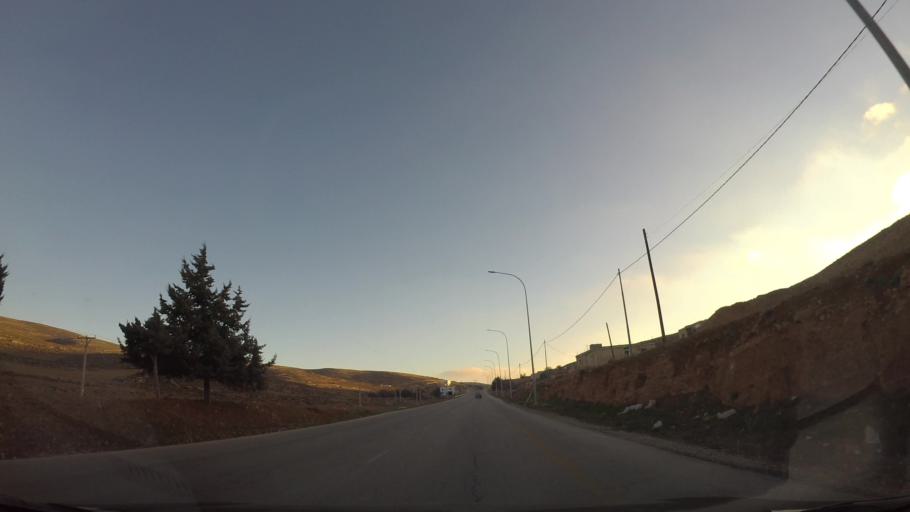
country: JO
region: Ma'an
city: Petra
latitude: 30.4253
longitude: 35.5134
